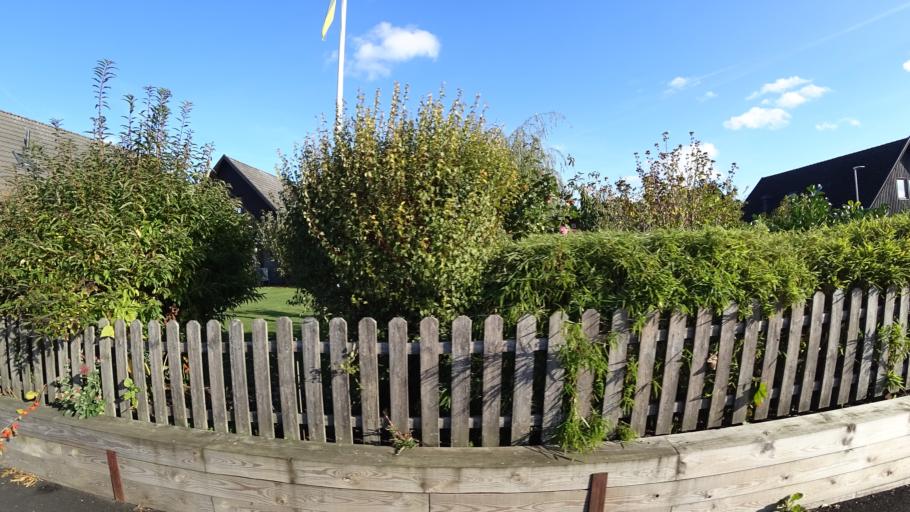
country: SE
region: Skane
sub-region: Staffanstorps Kommun
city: Hjaerup
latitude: 55.6684
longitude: 13.1446
